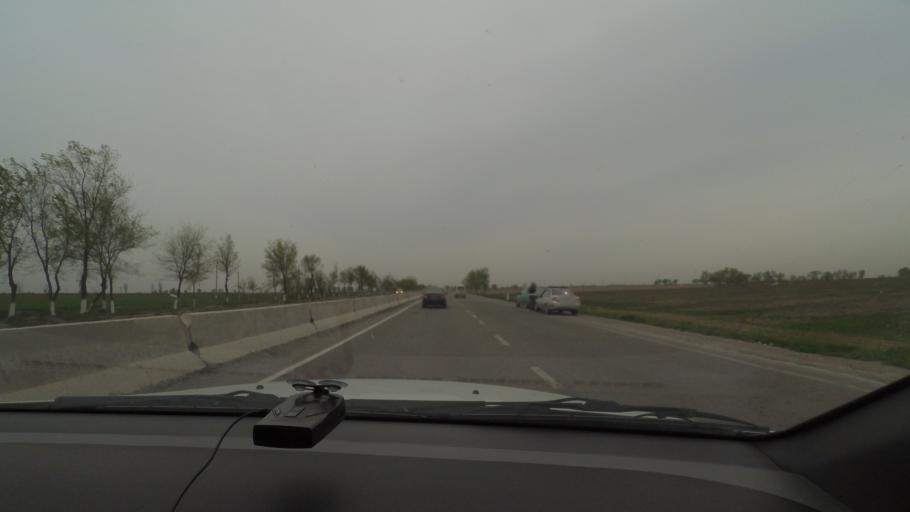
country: KZ
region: Ongtustik Qazaqstan
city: Myrzakent
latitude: 40.5288
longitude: 68.4423
